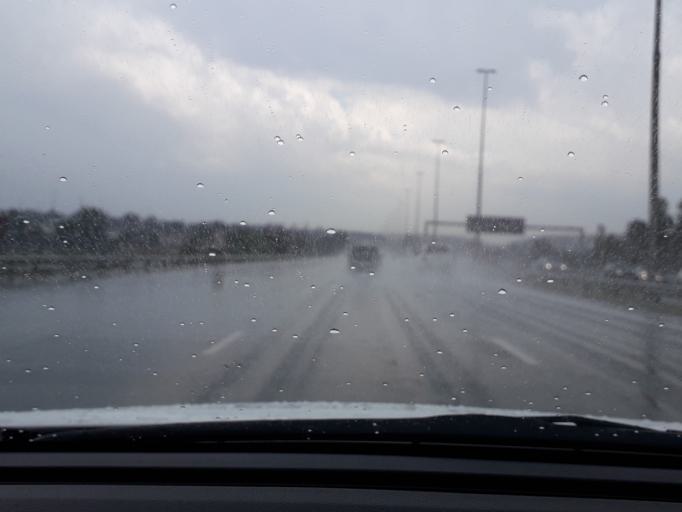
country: ZA
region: Gauteng
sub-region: City of Johannesburg Metropolitan Municipality
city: Roodepoort
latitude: -26.1930
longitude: 27.9500
